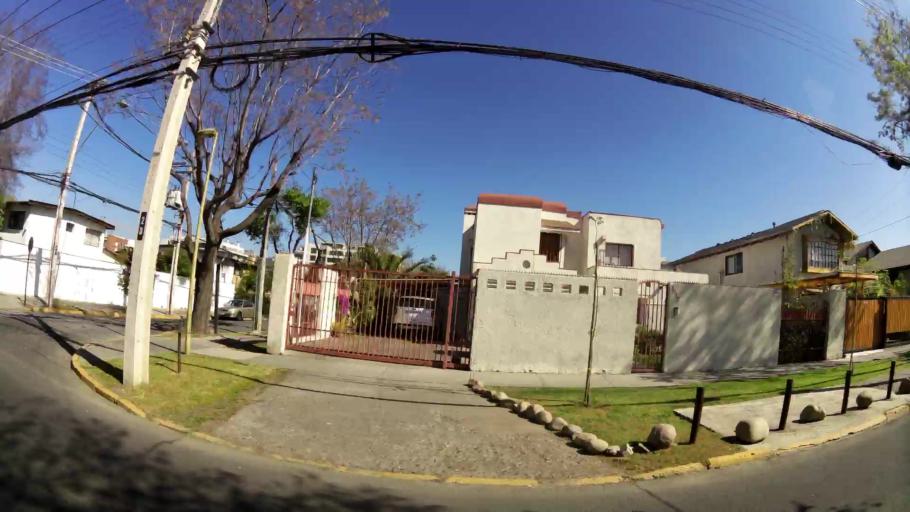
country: CL
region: Santiago Metropolitan
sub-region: Provincia de Santiago
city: Villa Presidente Frei, Nunoa, Santiago, Chile
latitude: -33.4036
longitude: -70.5532
